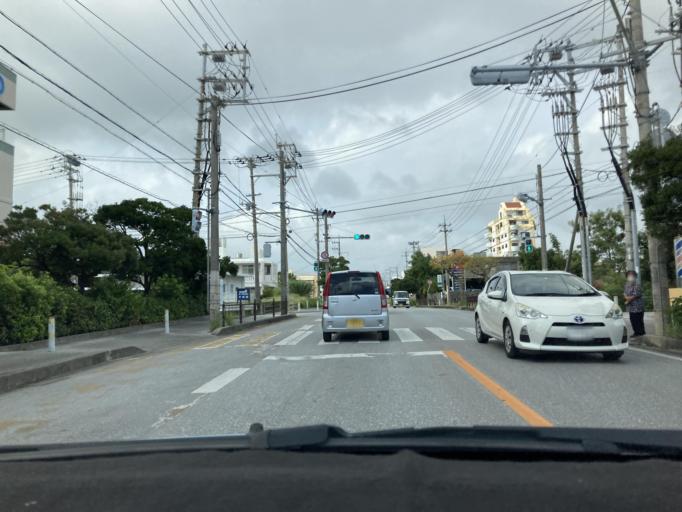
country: JP
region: Okinawa
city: Itoman
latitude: 26.1536
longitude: 127.6716
